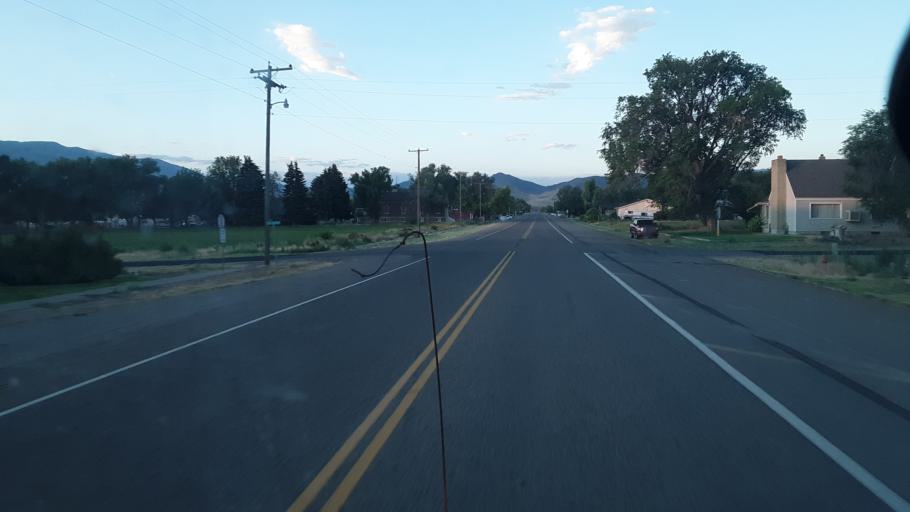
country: US
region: Utah
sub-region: Sevier County
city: Monroe
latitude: 38.6283
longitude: -112.2181
